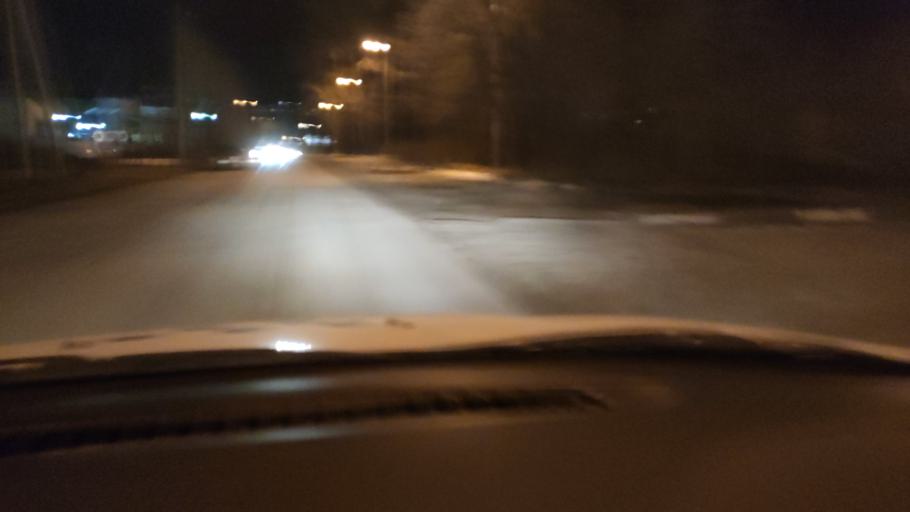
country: RU
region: Perm
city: Perm
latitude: 57.9766
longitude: 56.2813
